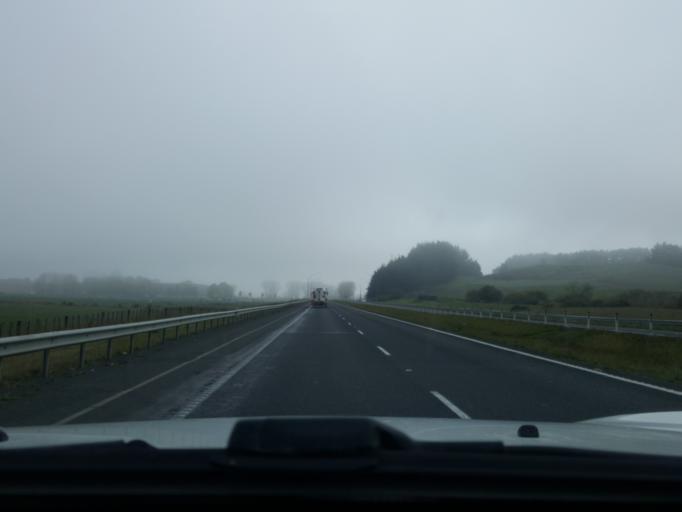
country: NZ
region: Waikato
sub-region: Waikato District
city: Te Kauwhata
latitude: -37.3429
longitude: 175.0669
